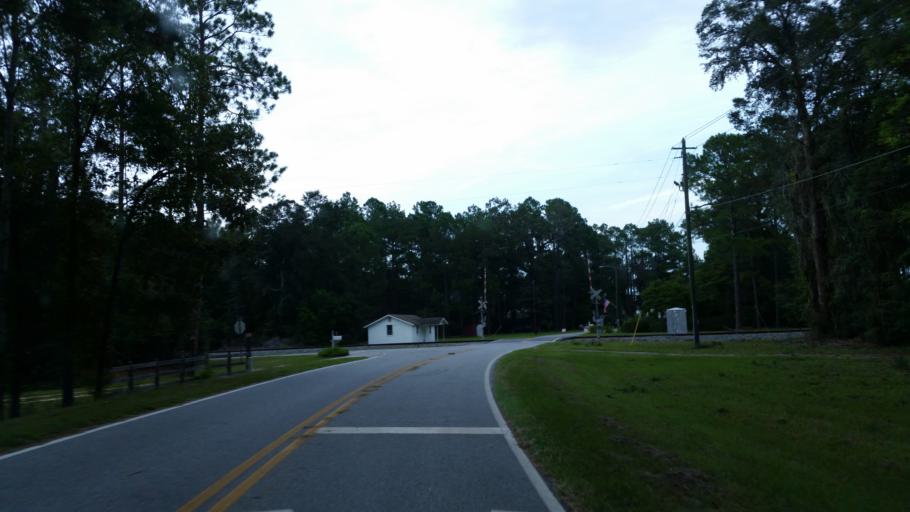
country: US
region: Georgia
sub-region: Lowndes County
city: Valdosta
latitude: 30.7473
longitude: -83.2268
